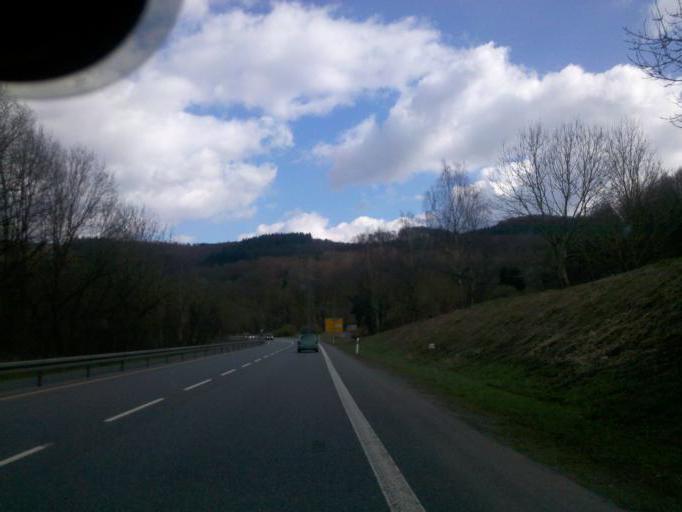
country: DE
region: Hesse
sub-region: Regierungsbezirk Giessen
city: Haiger
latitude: 50.7393
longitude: 8.2285
